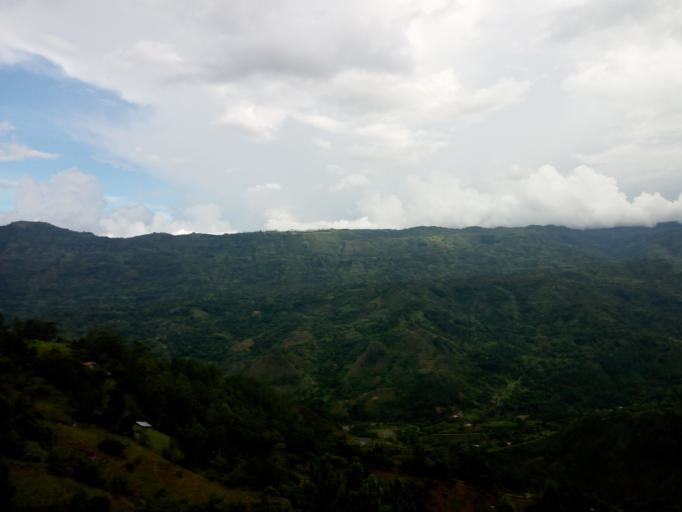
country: CO
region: Boyaca
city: Guateque
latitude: 4.9940
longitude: -73.4775
